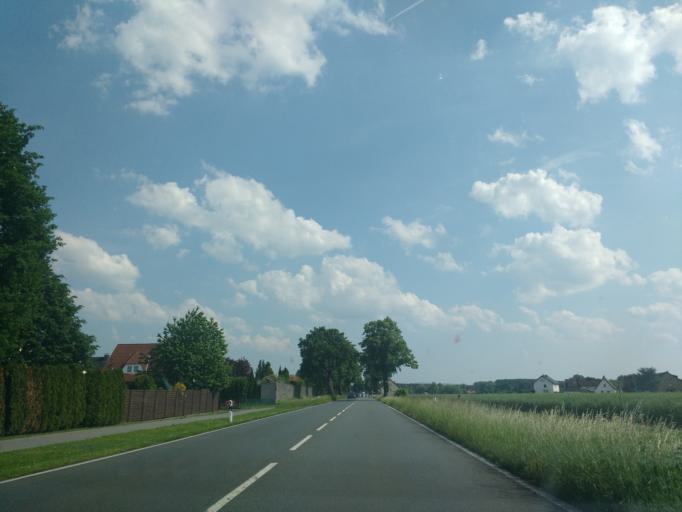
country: DE
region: North Rhine-Westphalia
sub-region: Regierungsbezirk Detmold
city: Lage
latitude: 52.0228
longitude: 8.7617
